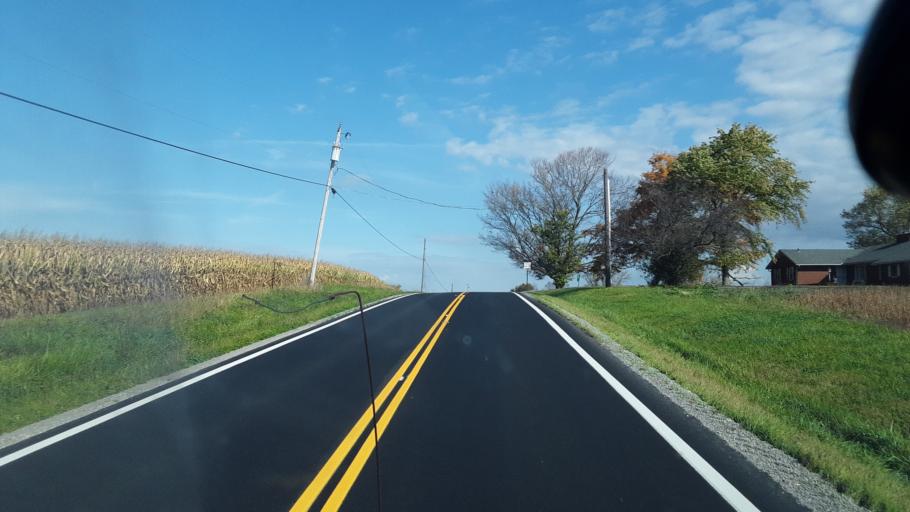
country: US
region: Ohio
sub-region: Highland County
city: Leesburg
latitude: 39.3099
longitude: -83.5883
